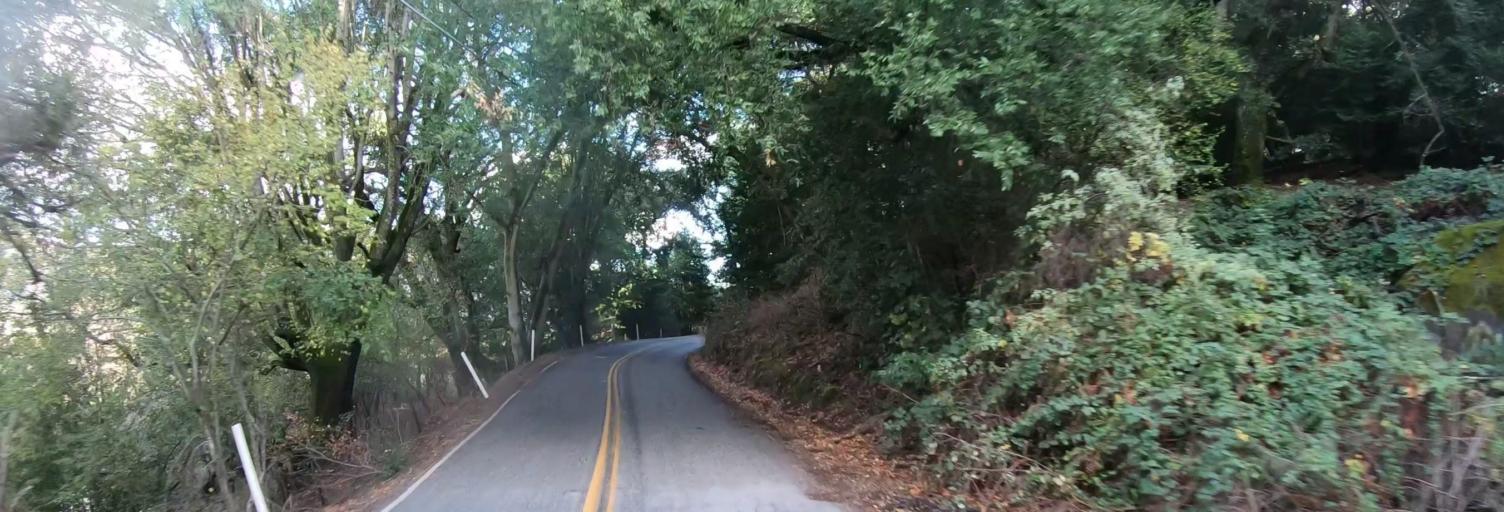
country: US
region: California
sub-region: Santa Clara County
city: East Foothills
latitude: 37.3492
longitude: -121.7303
